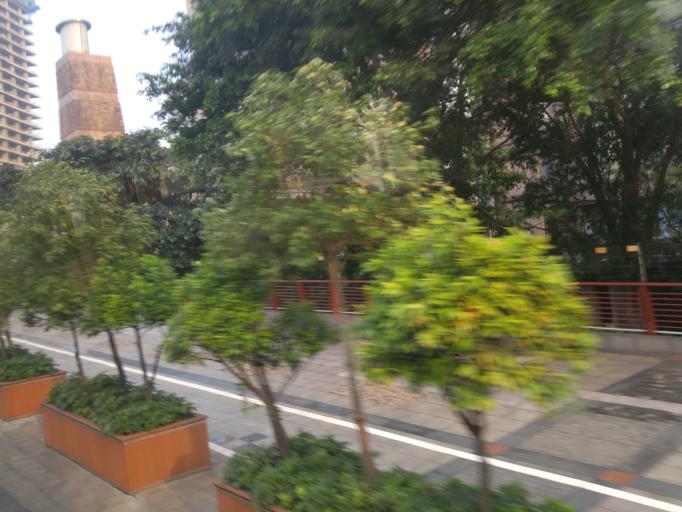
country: CN
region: Guangdong
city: Foshan
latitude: 23.0605
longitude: 113.1412
